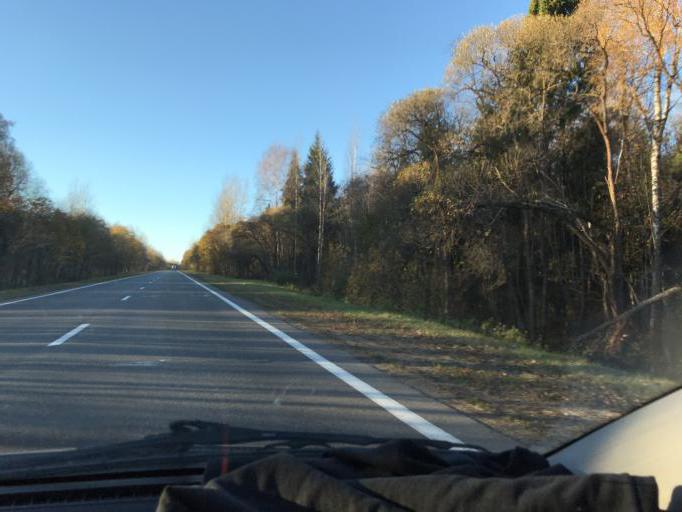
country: BY
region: Vitebsk
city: Vitebsk
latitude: 55.3549
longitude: 30.1885
